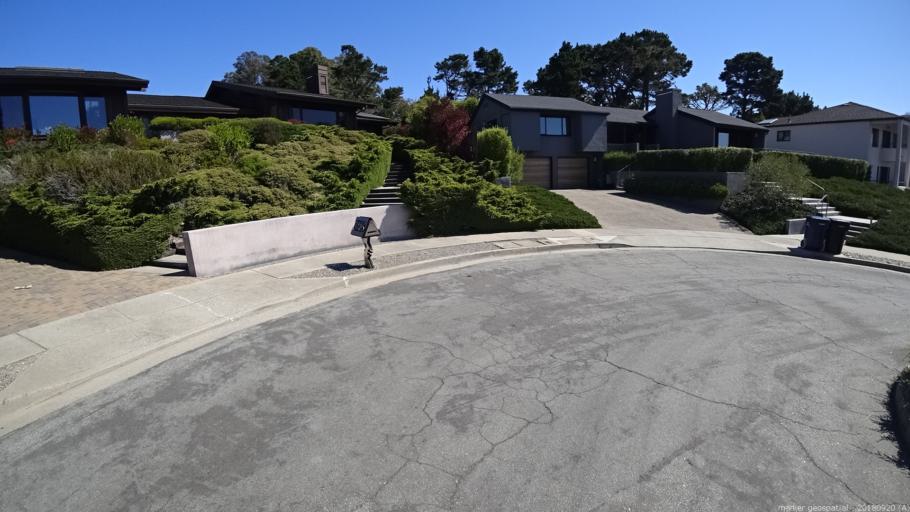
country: US
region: California
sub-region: Monterey County
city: Carmel-by-the-Sea
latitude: 36.5629
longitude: -121.9079
